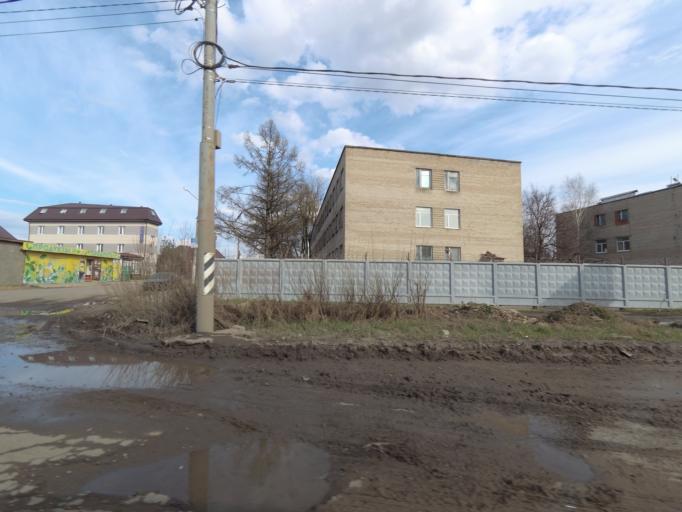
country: RU
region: Moskovskaya
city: Lobnya
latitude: 55.9903
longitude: 37.4162
